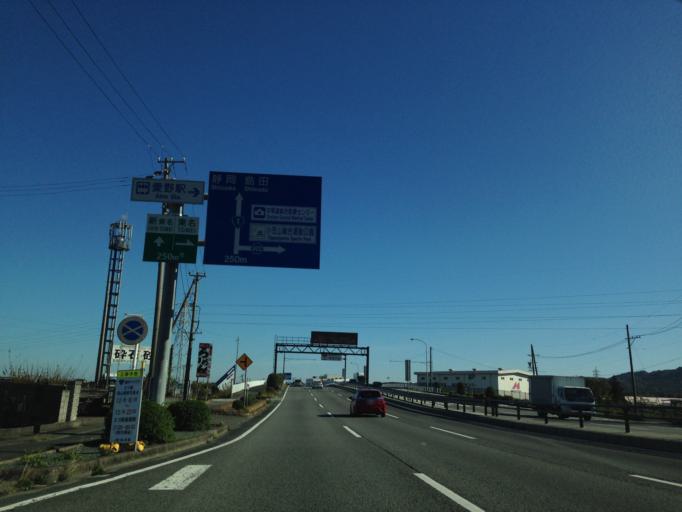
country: JP
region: Shizuoka
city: Fukuroi
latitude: 34.7629
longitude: 137.9653
